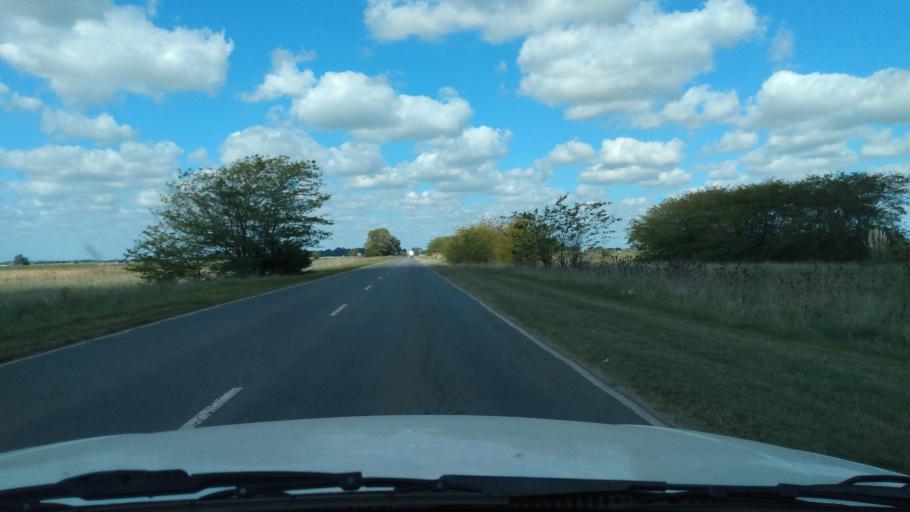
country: AR
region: Buenos Aires
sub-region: Partido de Navarro
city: Navarro
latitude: -34.9715
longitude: -59.3173
